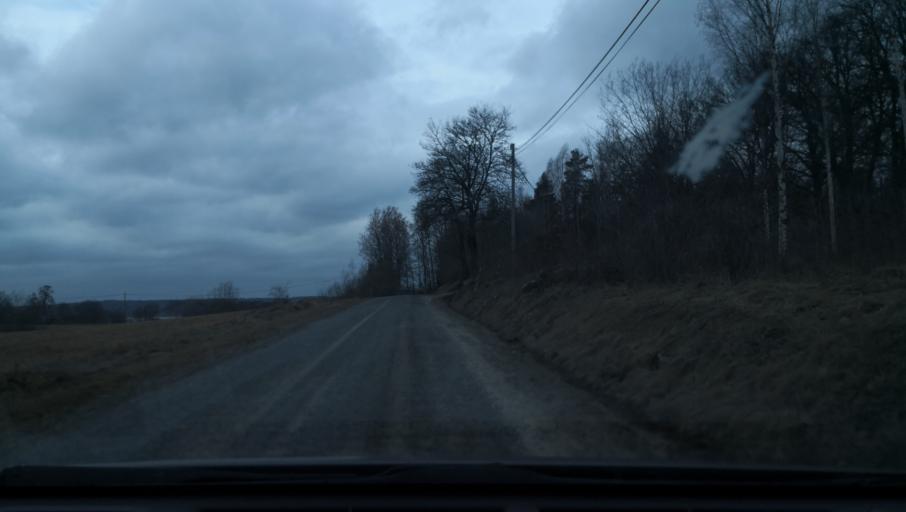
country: SE
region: Vaestmanland
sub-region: Kopings Kommun
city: Kolsva
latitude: 59.5846
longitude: 15.7125
